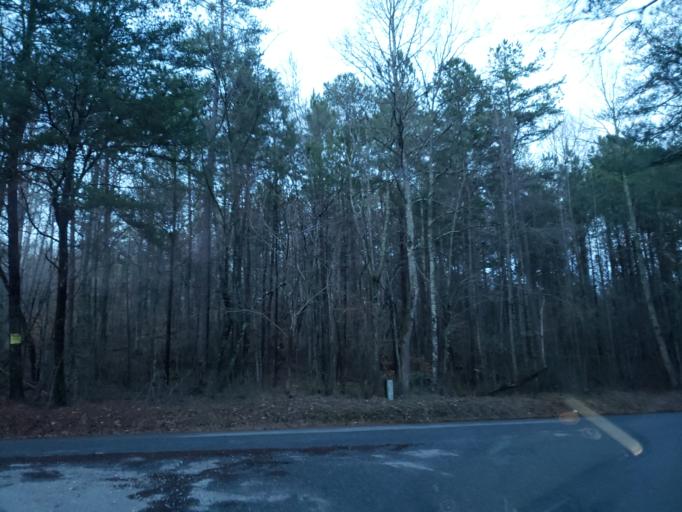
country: US
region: Georgia
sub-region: Cherokee County
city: Ball Ground
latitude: 34.2918
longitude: -84.3011
